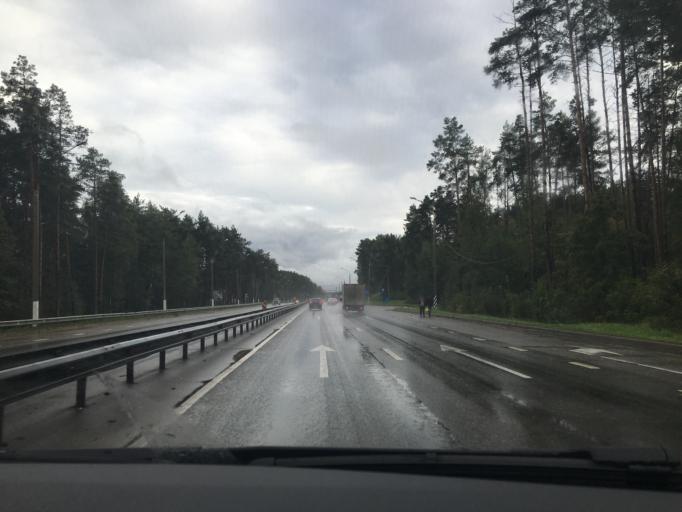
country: RU
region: Kaluga
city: Obninsk
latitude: 55.0606
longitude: 36.6206
